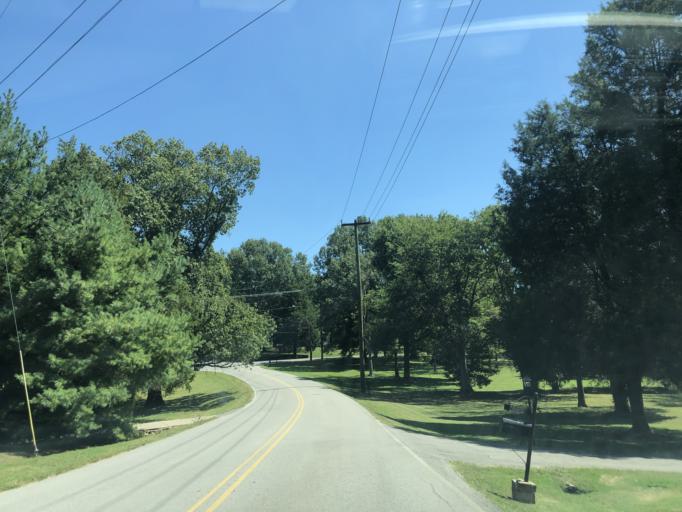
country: US
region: Tennessee
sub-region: Davidson County
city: Forest Hills
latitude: 36.0642
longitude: -86.8421
